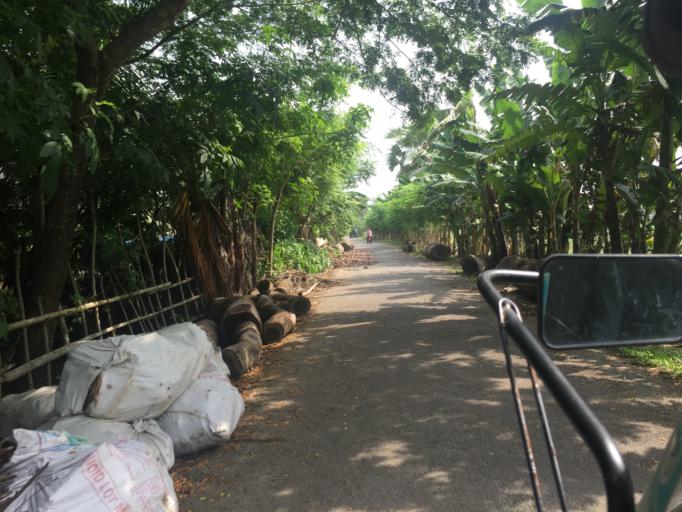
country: BD
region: Barisal
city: Mathba
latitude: 22.2532
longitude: 89.9124
